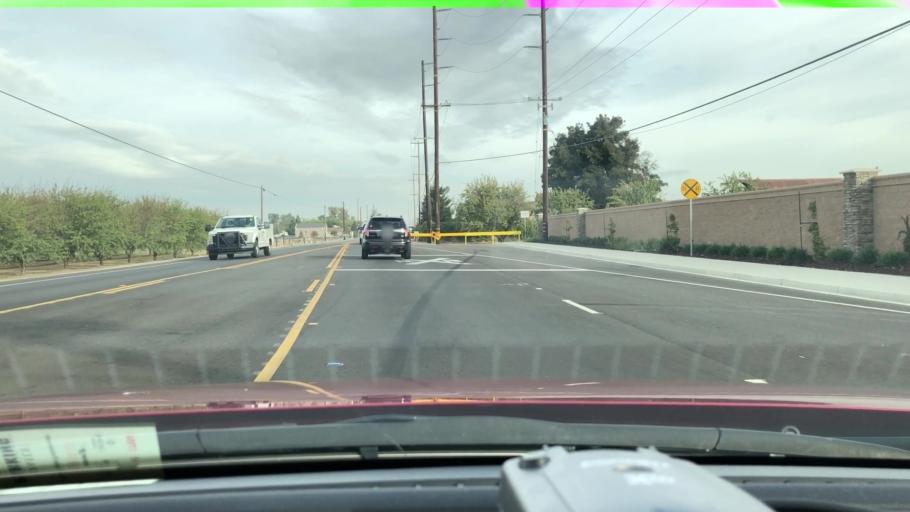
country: US
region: California
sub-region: San Joaquin County
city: Lathrop
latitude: 37.8142
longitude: -121.2531
